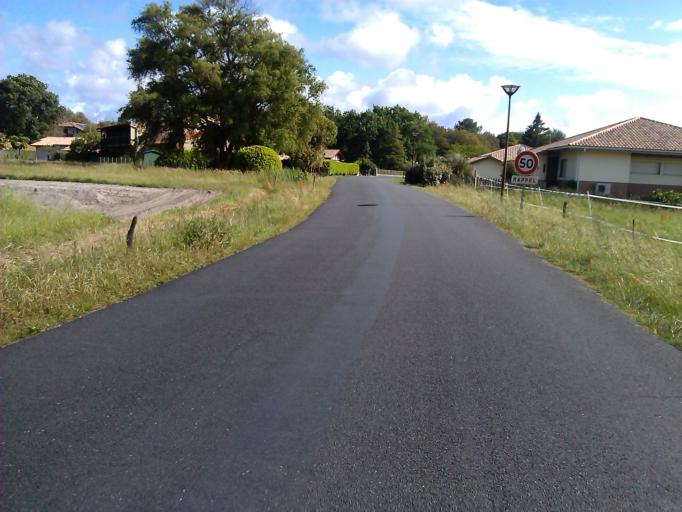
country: FR
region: Aquitaine
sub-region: Departement des Landes
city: Leon
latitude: 43.8543
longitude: -1.3590
